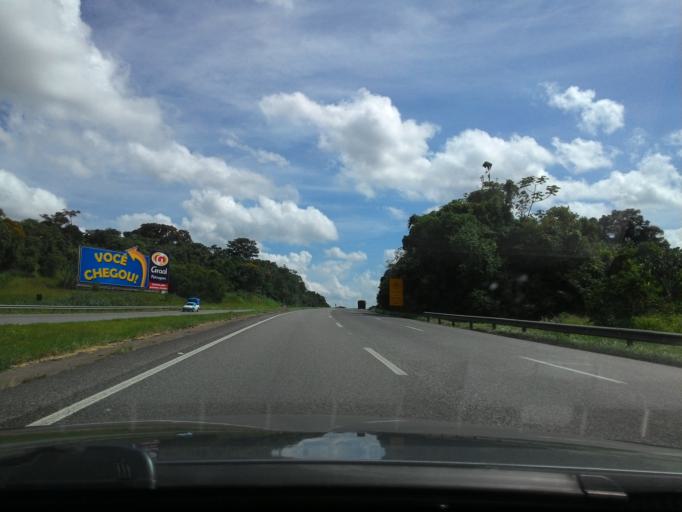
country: BR
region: Sao Paulo
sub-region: Pariquera-Acu
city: Pariquera Acu
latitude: -24.6078
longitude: -47.8805
